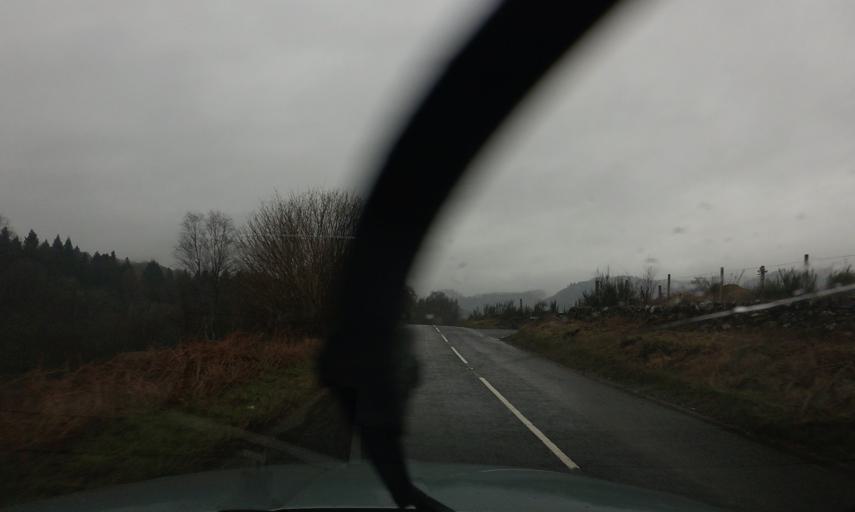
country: GB
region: Scotland
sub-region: Stirling
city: Balfron
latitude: 56.1638
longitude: -4.3634
